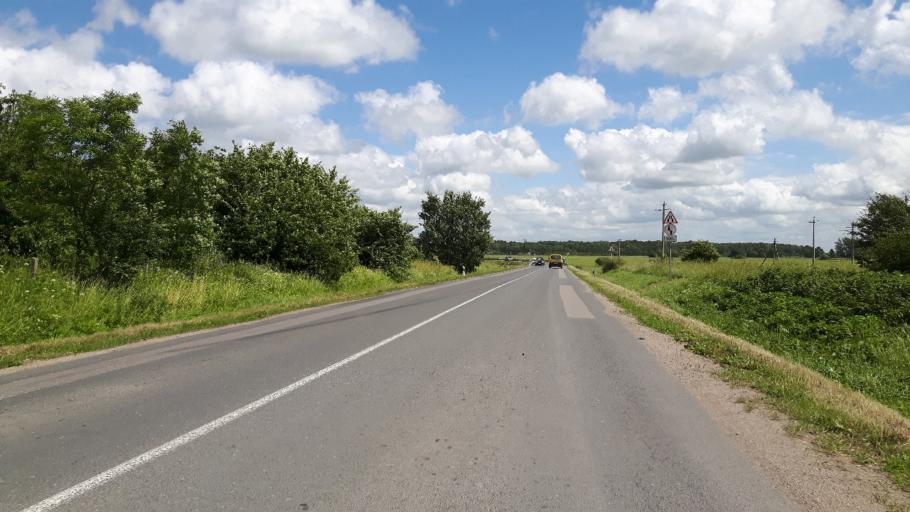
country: RU
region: Kaliningrad
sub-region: Zelenogradskiy Rayon
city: Zelenogradsk
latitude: 54.9289
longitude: 20.4186
